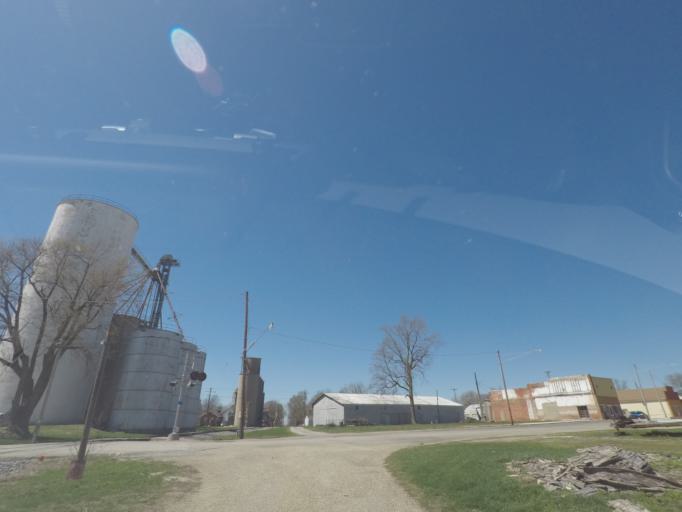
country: US
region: Illinois
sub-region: Macon County
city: Warrensburg
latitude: 39.9656
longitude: -89.1613
